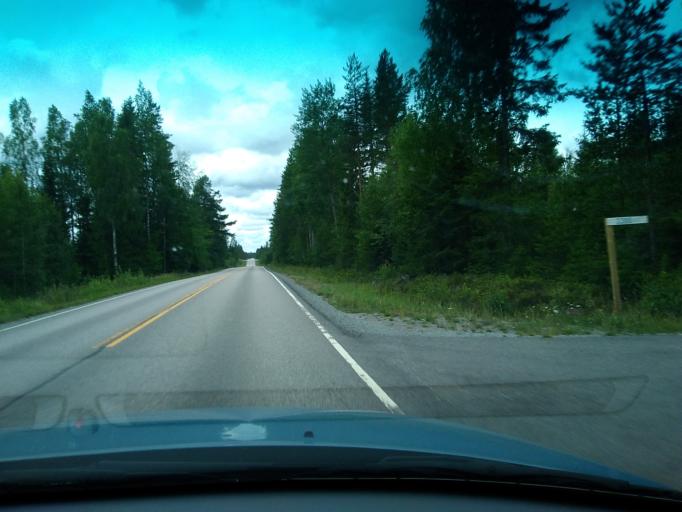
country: FI
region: Central Finland
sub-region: Saarijaervi-Viitasaari
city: Pylkoenmaeki
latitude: 62.6139
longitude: 24.7197
